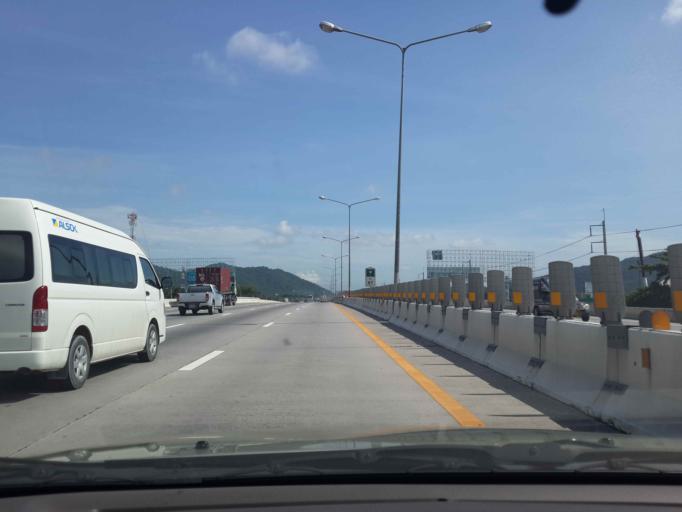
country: TH
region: Chon Buri
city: Si Racha
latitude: 13.2295
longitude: 101.0012
